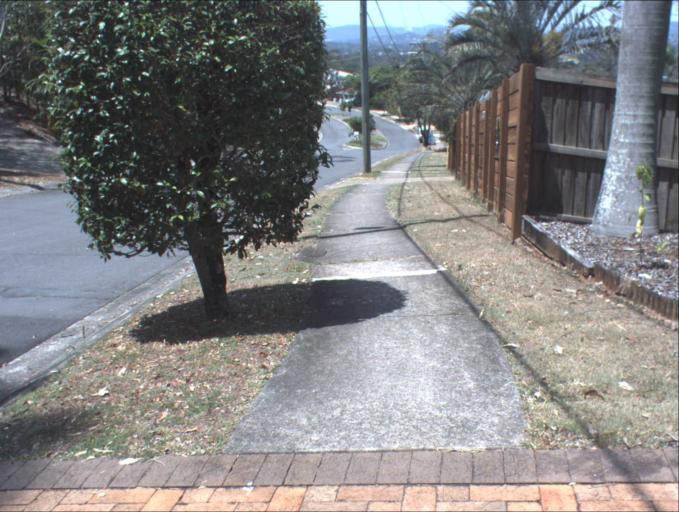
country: AU
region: Queensland
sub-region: Logan
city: Slacks Creek
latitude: -27.6601
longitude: 153.1912
